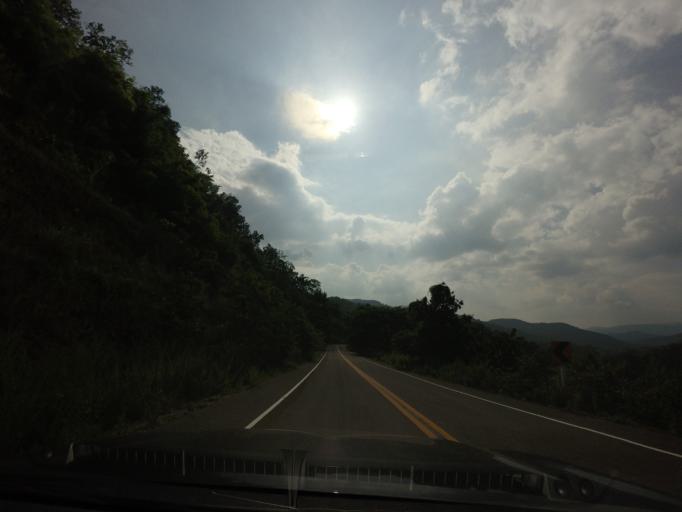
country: TH
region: Nan
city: Na Noi
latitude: 18.2802
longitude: 100.9496
